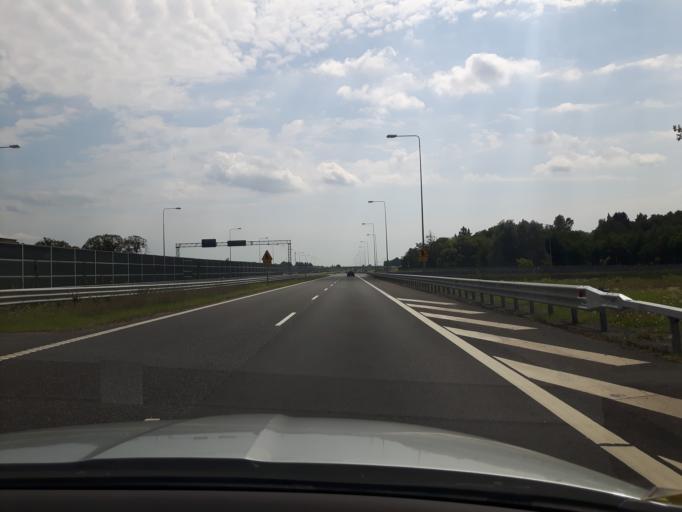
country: PL
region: Warmian-Masurian Voivodeship
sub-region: Powiat olsztynski
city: Olsztynek
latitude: 53.4997
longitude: 20.3126
